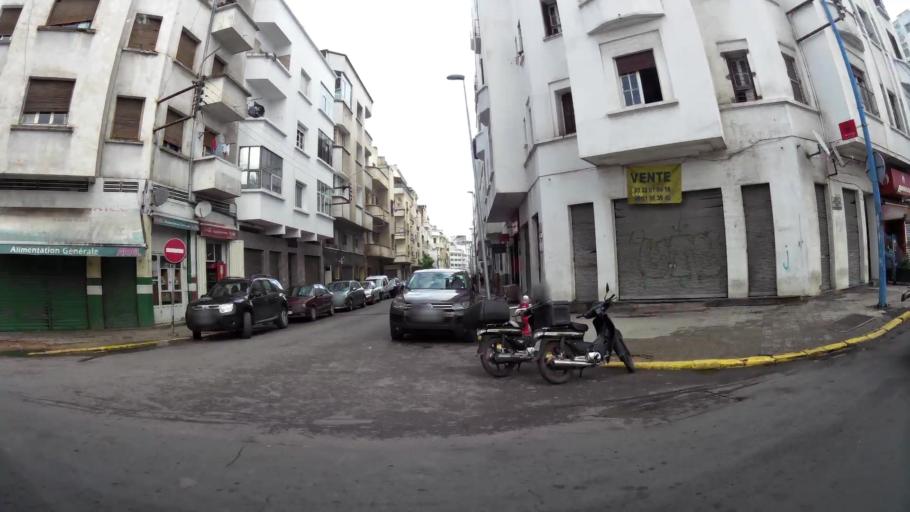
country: MA
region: Grand Casablanca
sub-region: Casablanca
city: Casablanca
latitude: 33.5832
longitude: -7.6217
